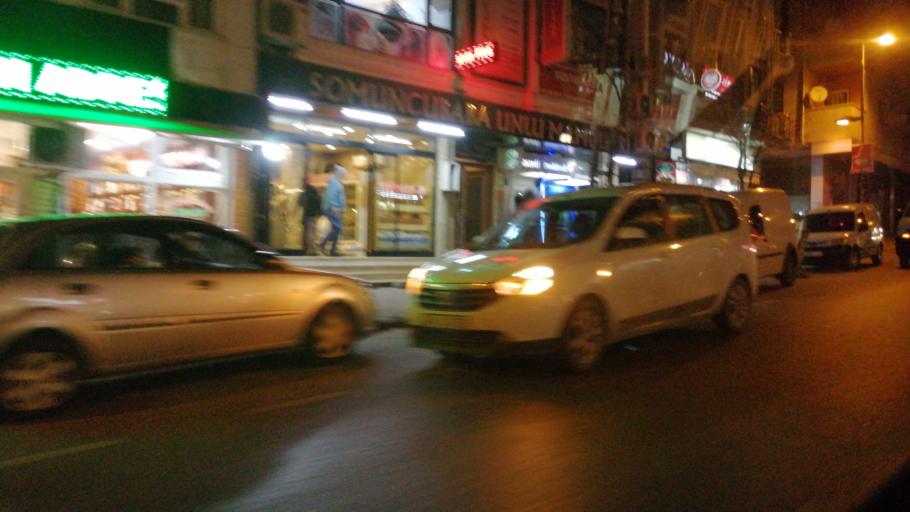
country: TR
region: Istanbul
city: Umraniye
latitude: 41.0136
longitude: 29.1283
